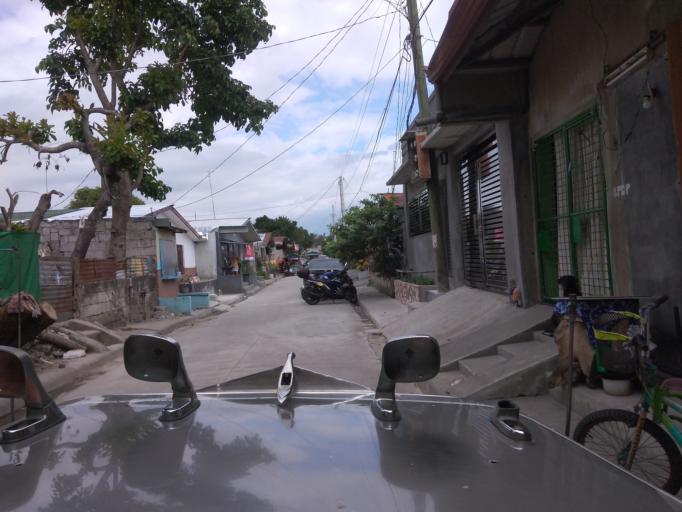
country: PH
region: Central Luzon
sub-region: Province of Pampanga
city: Pandacaqui
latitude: 15.1766
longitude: 120.6529
